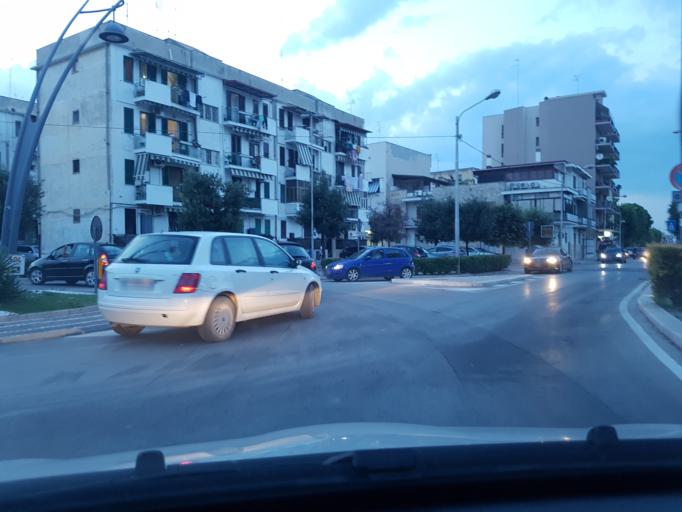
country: IT
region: Apulia
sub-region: Provincia di Foggia
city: Cerignola
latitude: 41.2607
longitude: 15.9048
